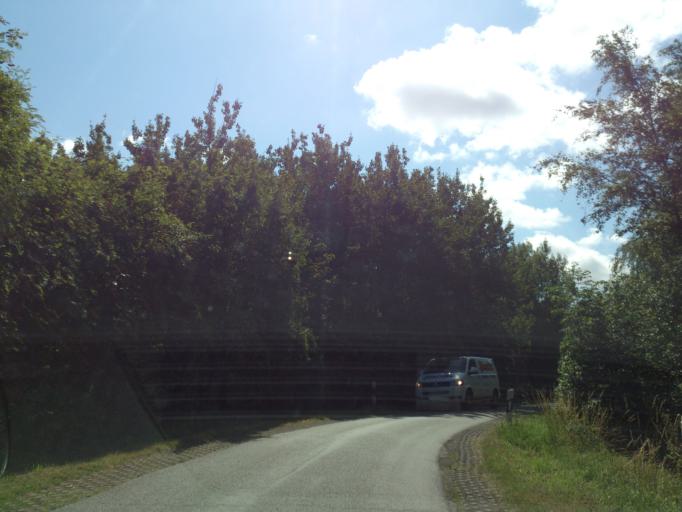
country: DE
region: Schleswig-Holstein
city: Sankt Peter-Ording
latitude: 54.3122
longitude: 8.6319
